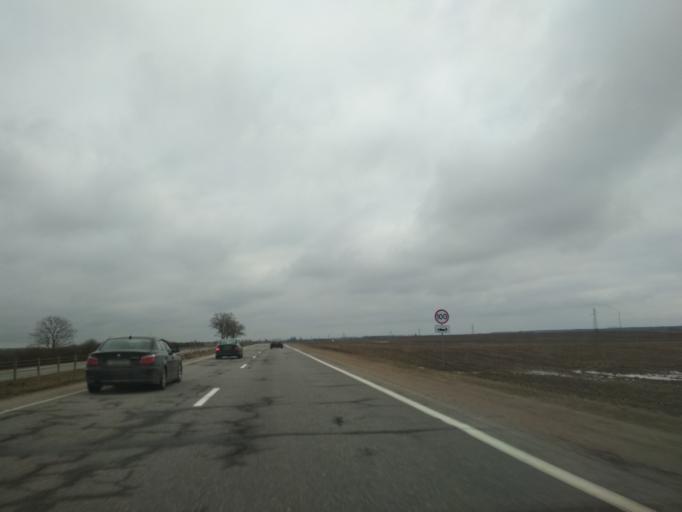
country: BY
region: Minsk
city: Dukora
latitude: 53.6838
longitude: 27.9162
